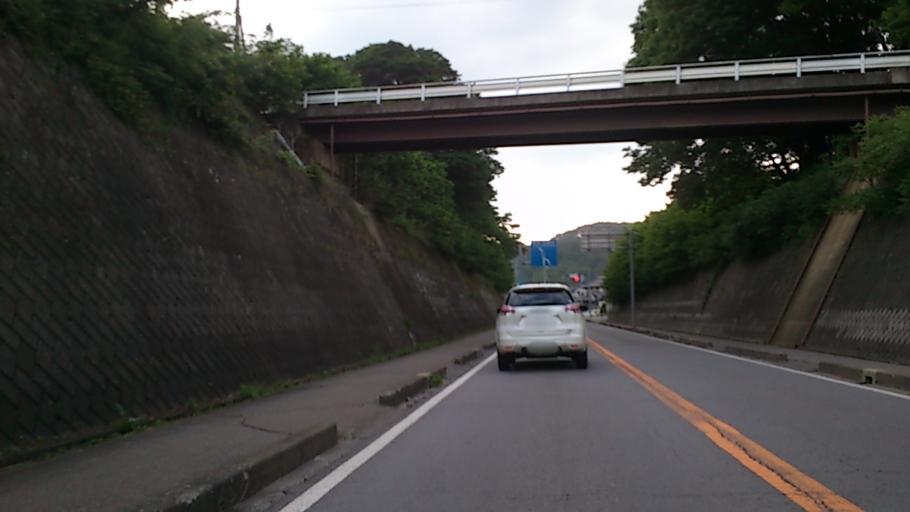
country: JP
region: Nagano
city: Komoro
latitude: 36.2699
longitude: 138.3898
